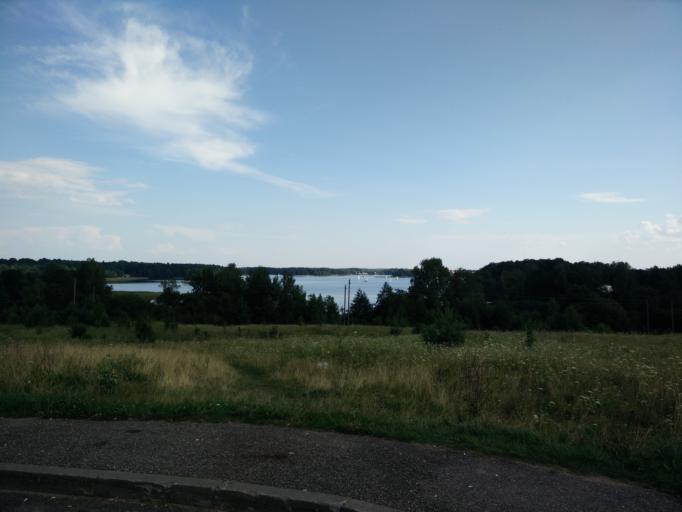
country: LT
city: Trakai
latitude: 54.6729
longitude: 24.9317
